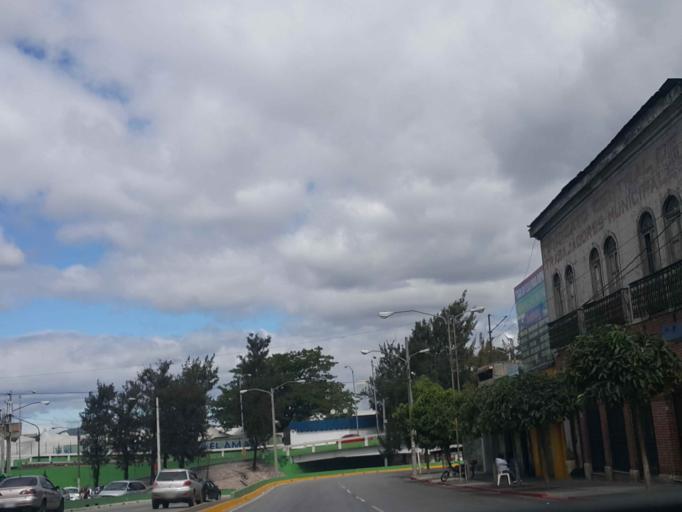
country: GT
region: Guatemala
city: Guatemala City
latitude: 14.6293
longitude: -90.5180
